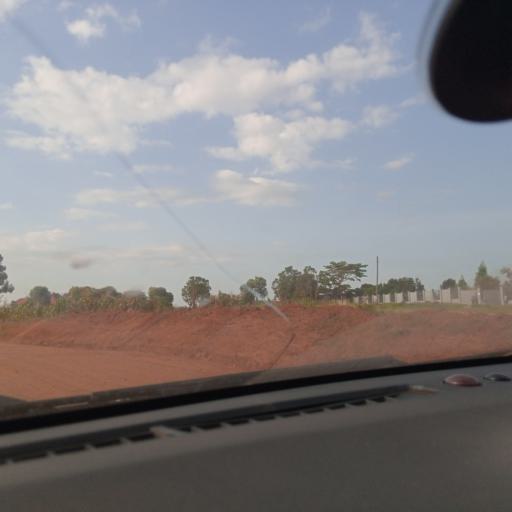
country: UG
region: Central Region
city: Masaka
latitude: -0.3587
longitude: 31.7442
